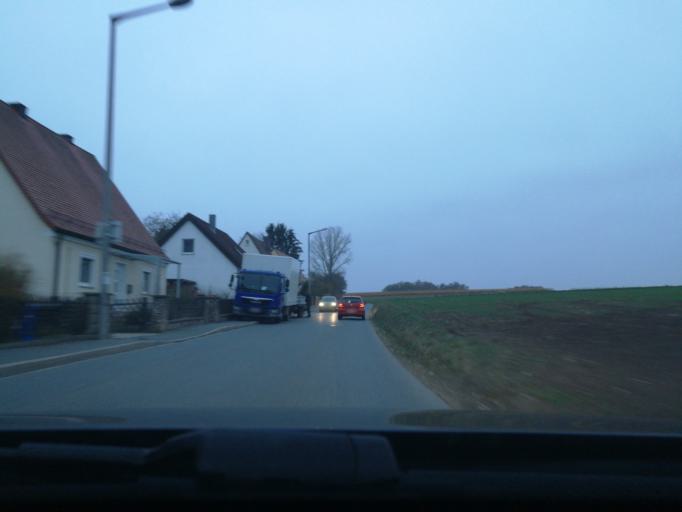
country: DE
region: Bavaria
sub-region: Regierungsbezirk Mittelfranken
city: Obermichelbach
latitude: 49.5086
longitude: 10.9342
